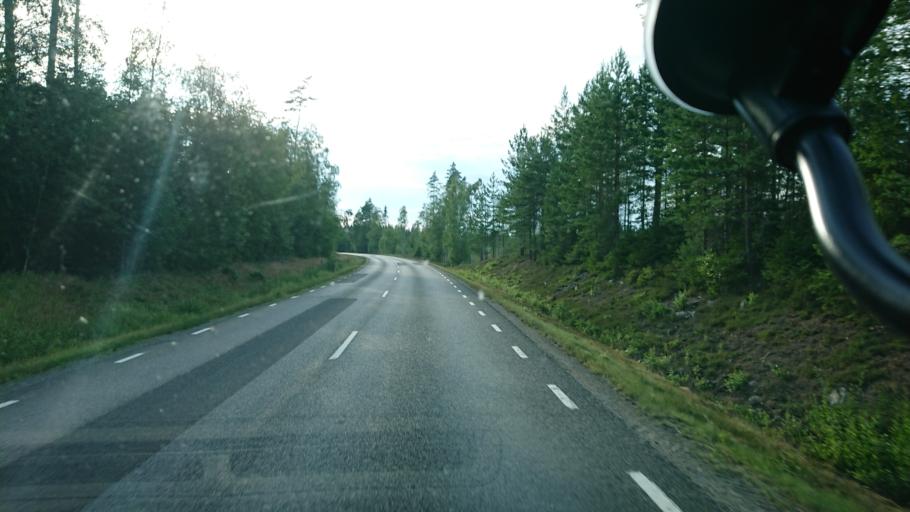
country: SE
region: Kronoberg
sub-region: Vaxjo Kommun
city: Braas
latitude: 57.0238
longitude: 15.0061
